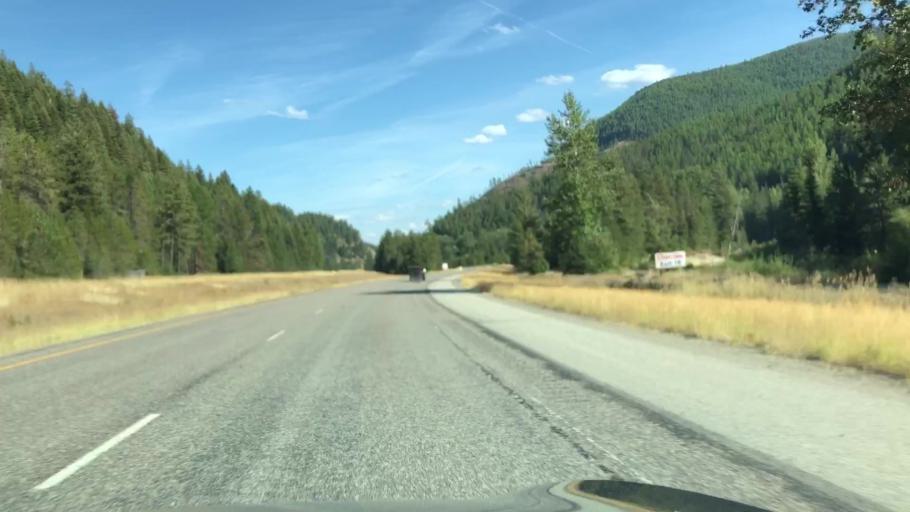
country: US
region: Montana
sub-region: Sanders County
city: Thompson Falls
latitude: 47.4070
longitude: -115.4926
